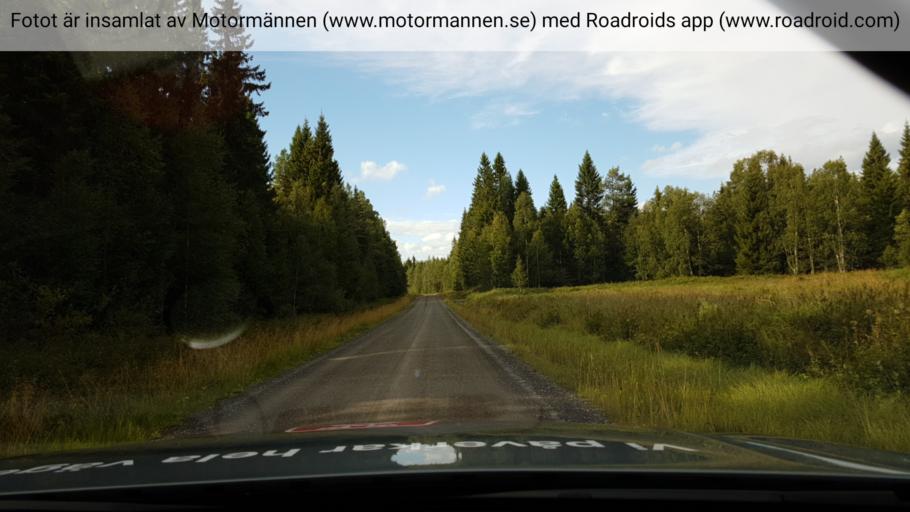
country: SE
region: Jaemtland
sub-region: OEstersunds Kommun
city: Lit
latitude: 63.3126
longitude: 15.2389
